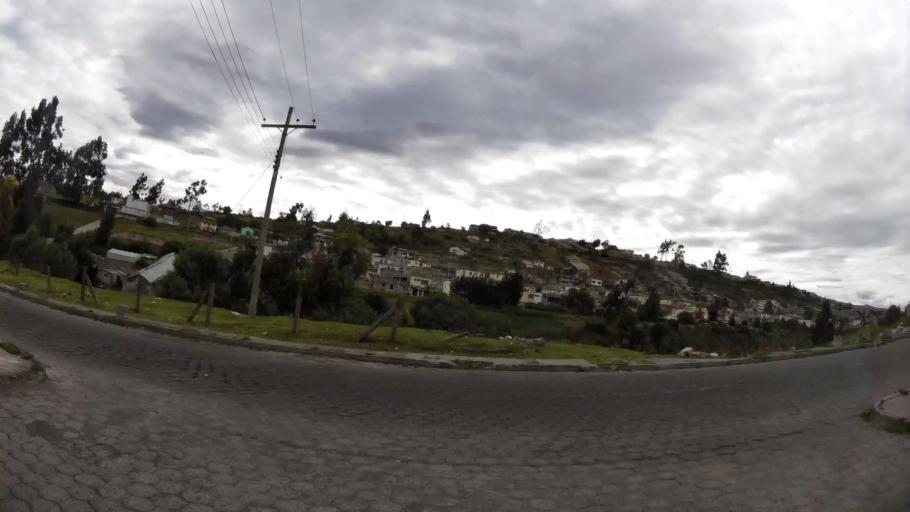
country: EC
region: Cotopaxi
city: Latacunga
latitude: -0.9392
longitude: -78.6221
